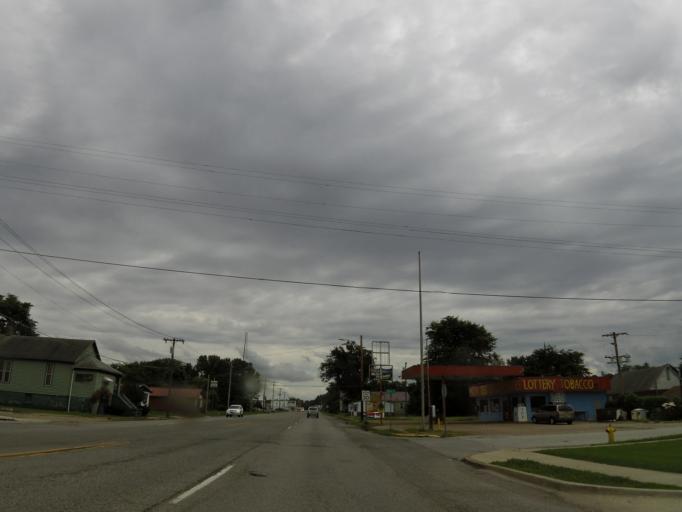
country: US
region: Illinois
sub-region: Alexander County
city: Cairo
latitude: 37.0109
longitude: -89.1801
